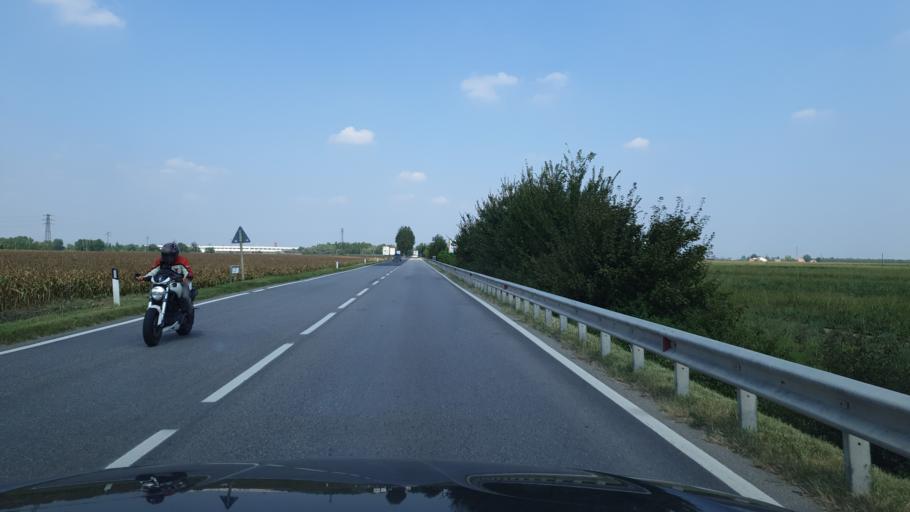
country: IT
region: Veneto
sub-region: Provincia di Rovigo
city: Bosaro
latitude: 45.0165
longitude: 11.7697
